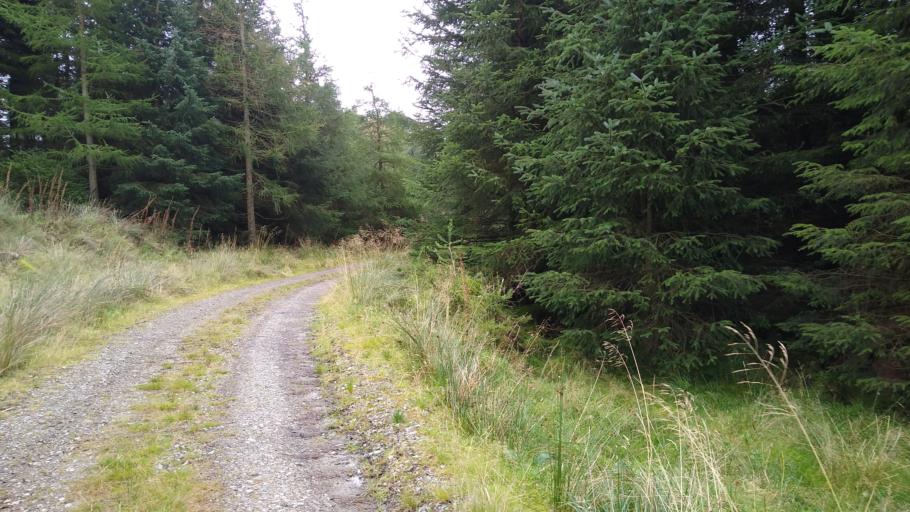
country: GB
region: England
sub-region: Cumbria
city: Keswick
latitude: 54.5617
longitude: -3.0817
